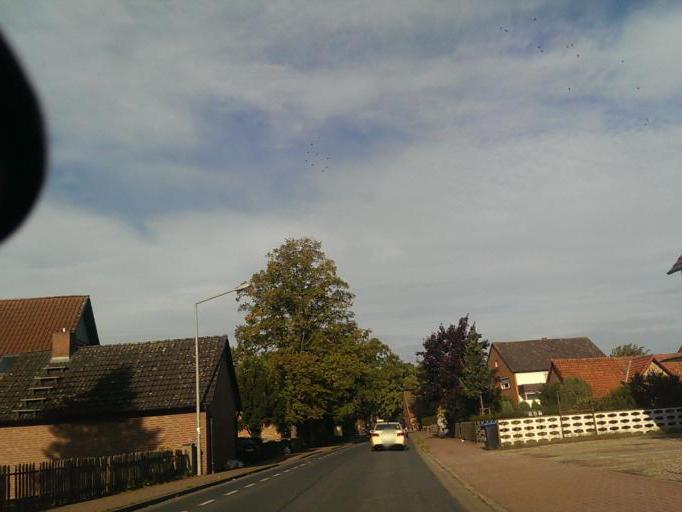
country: DE
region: Lower Saxony
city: Garbsen-Mitte
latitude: 52.4579
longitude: 9.5700
